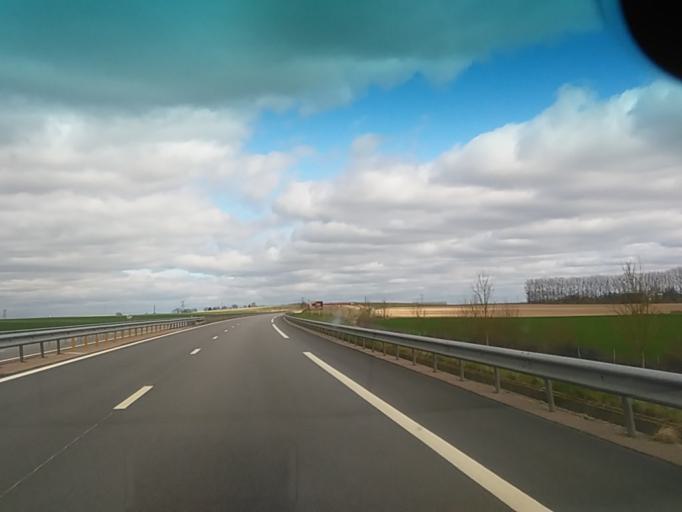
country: FR
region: Haute-Normandie
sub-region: Departement de l'Eure
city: Bourg-Achard
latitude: 49.2978
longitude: 0.7923
